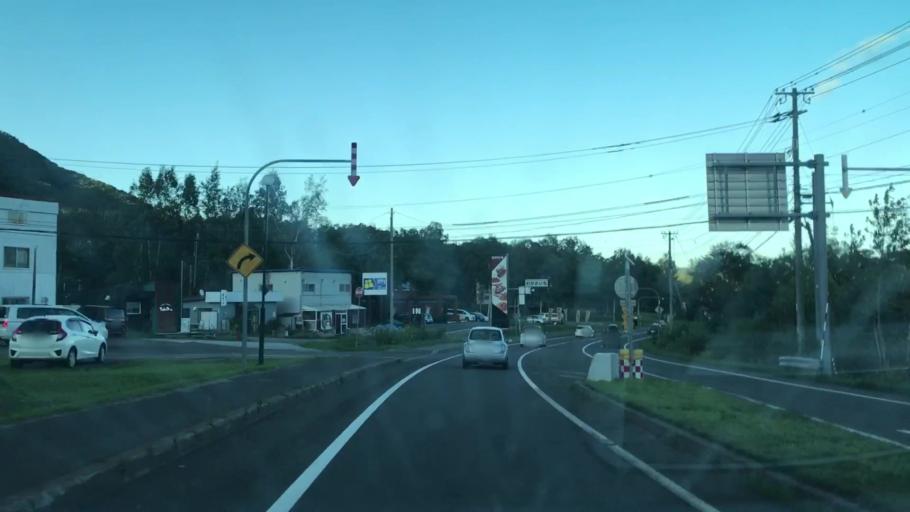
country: JP
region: Hokkaido
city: Niseko Town
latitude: 42.7522
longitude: 140.9044
